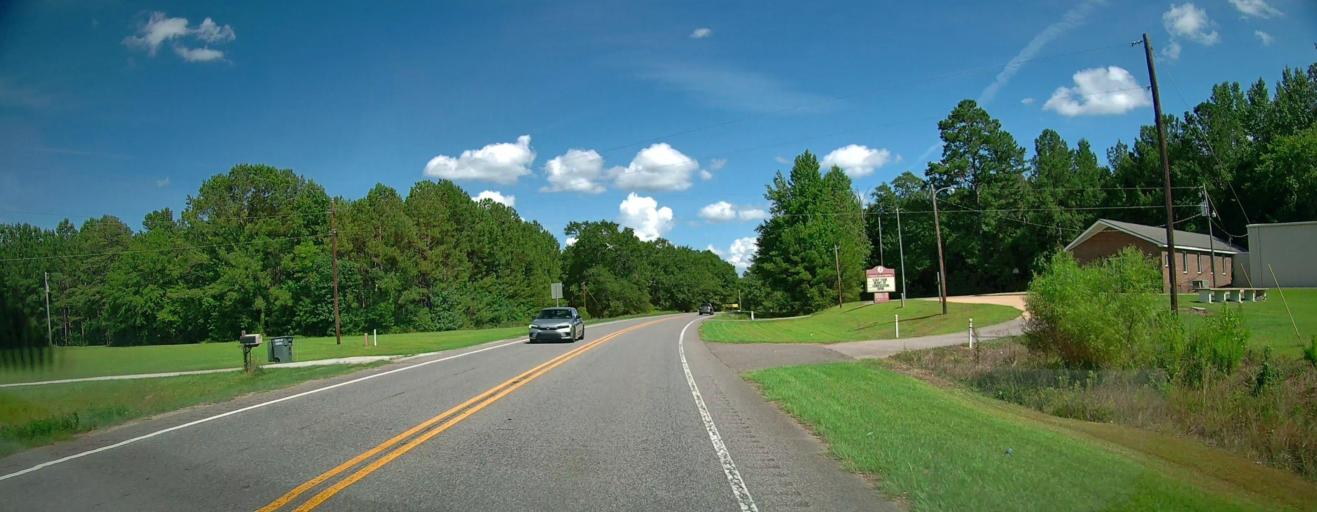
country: US
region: Alabama
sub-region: Pickens County
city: Gordo
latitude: 33.3318
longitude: -87.9155
